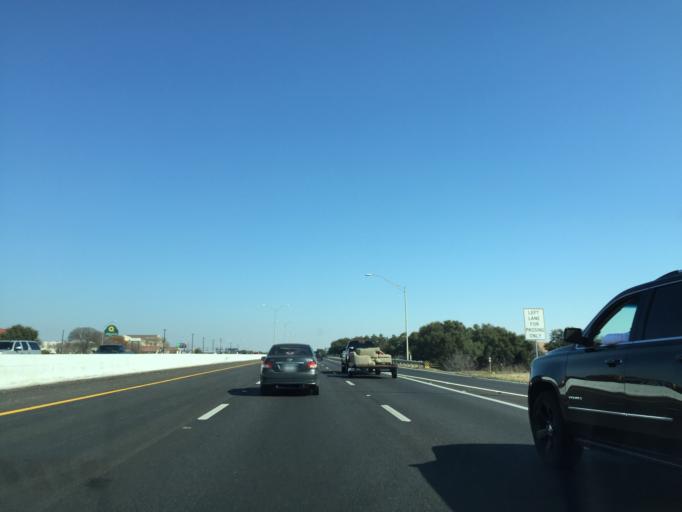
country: US
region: Texas
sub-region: Williamson County
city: Georgetown
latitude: 30.6518
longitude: -97.6780
